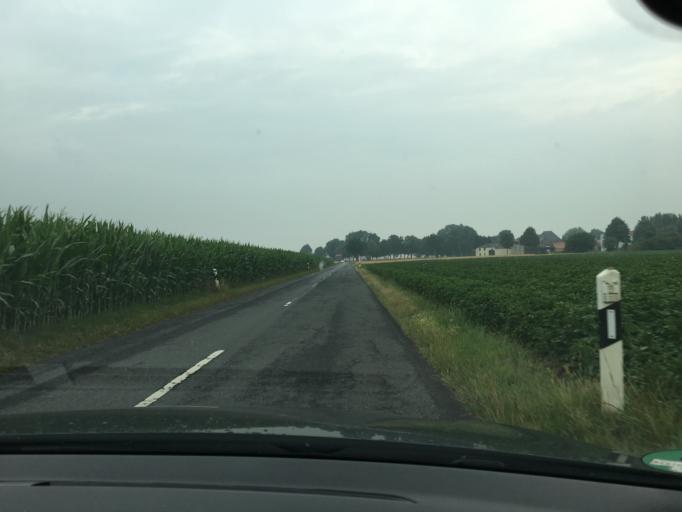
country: DE
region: North Rhine-Westphalia
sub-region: Regierungsbezirk Koln
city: Titz
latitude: 50.9741
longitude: 6.4084
